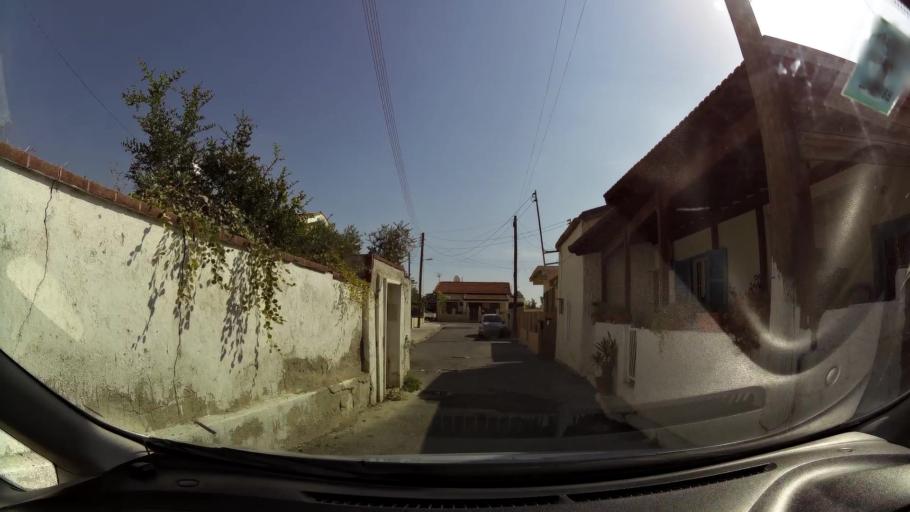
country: CY
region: Larnaka
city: Aradippou
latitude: 34.9537
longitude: 33.5935
